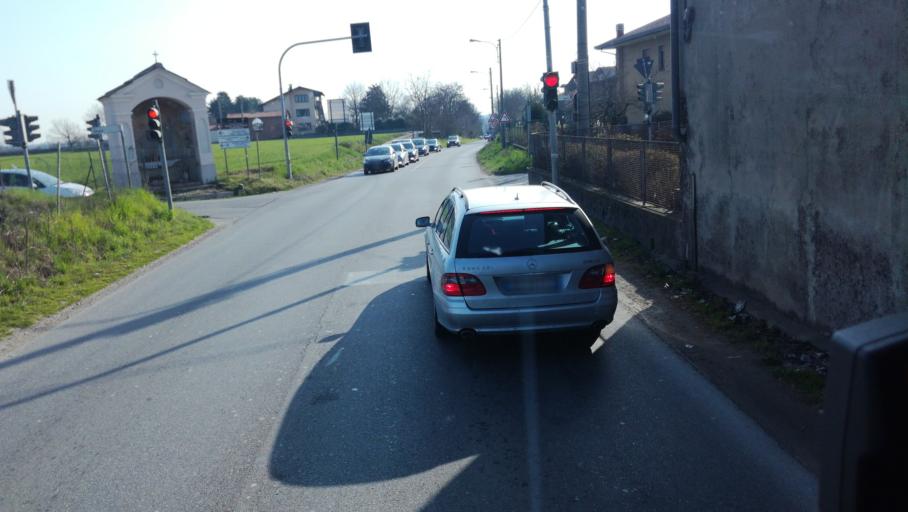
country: IT
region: Piedmont
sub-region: Provincia di Novara
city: Oleggio
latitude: 45.5920
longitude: 8.6551
